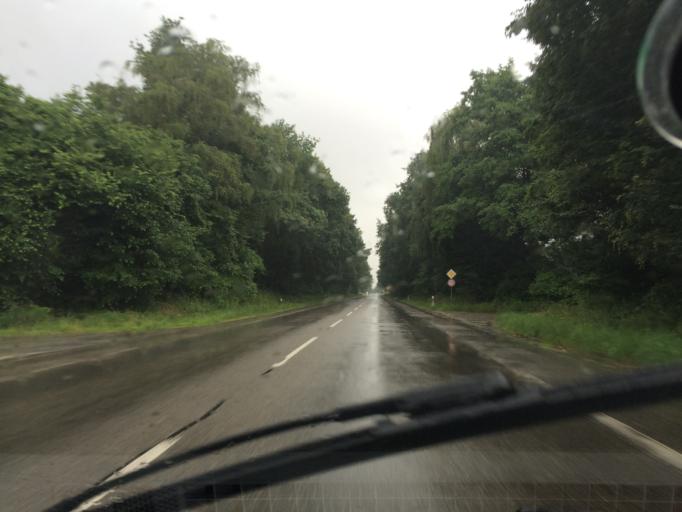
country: DE
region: North Rhine-Westphalia
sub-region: Regierungsbezirk Munster
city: Haltern
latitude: 51.7636
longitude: 7.1985
